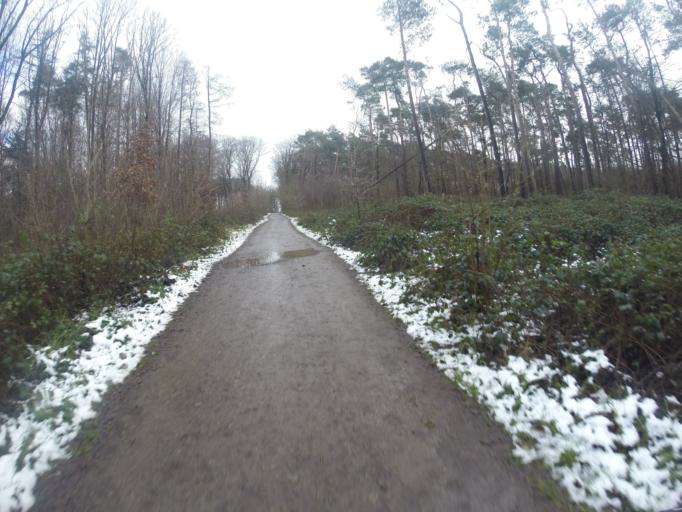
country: BE
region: Flanders
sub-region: Provincie Oost-Vlaanderen
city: Zomergem
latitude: 51.1368
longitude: 3.5167
